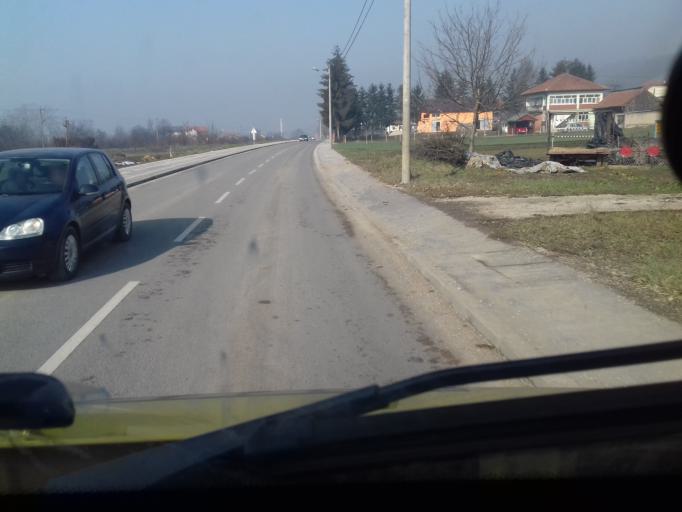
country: BA
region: Federation of Bosnia and Herzegovina
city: Mahala
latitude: 43.9776
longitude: 18.2414
